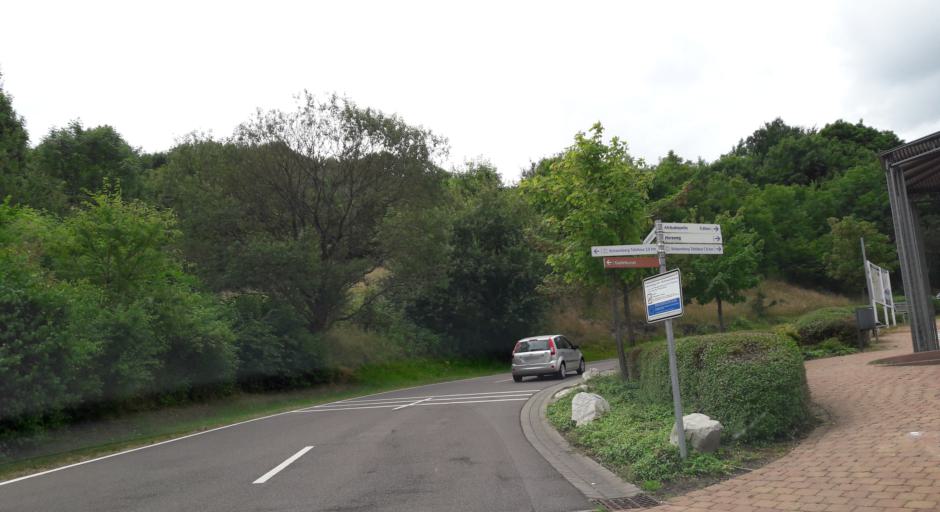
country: DE
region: Saarland
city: Tholey
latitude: 49.4893
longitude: 7.0318
